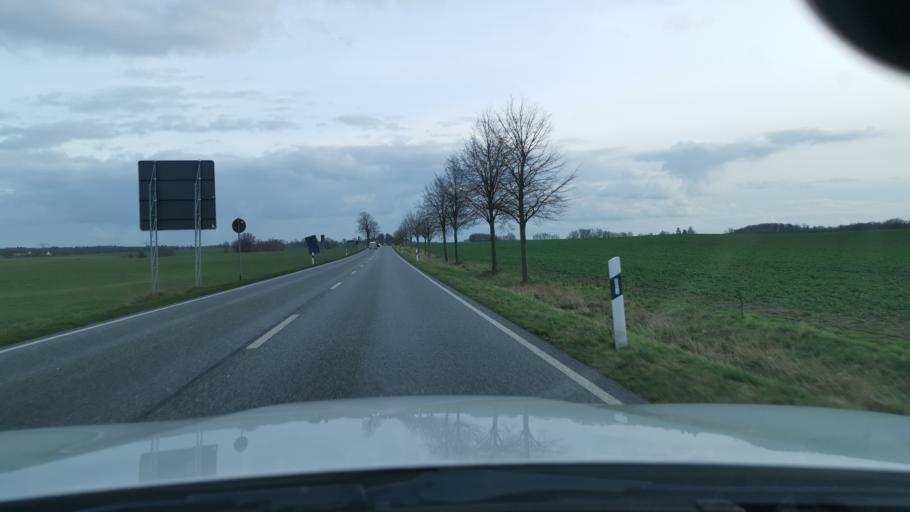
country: DE
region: Mecklenburg-Vorpommern
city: Dummerstorf
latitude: 53.9709
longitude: 12.2872
